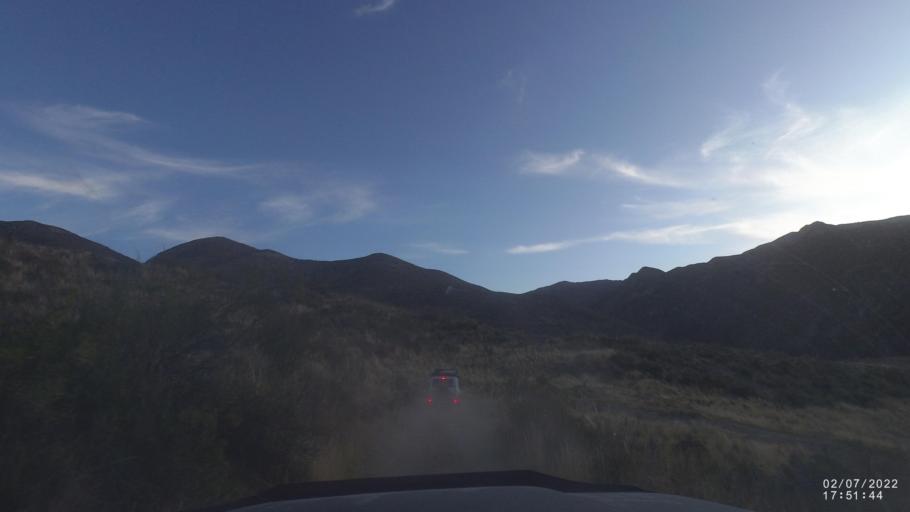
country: BO
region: Cochabamba
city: Irpa Irpa
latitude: -17.8475
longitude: -66.6181
